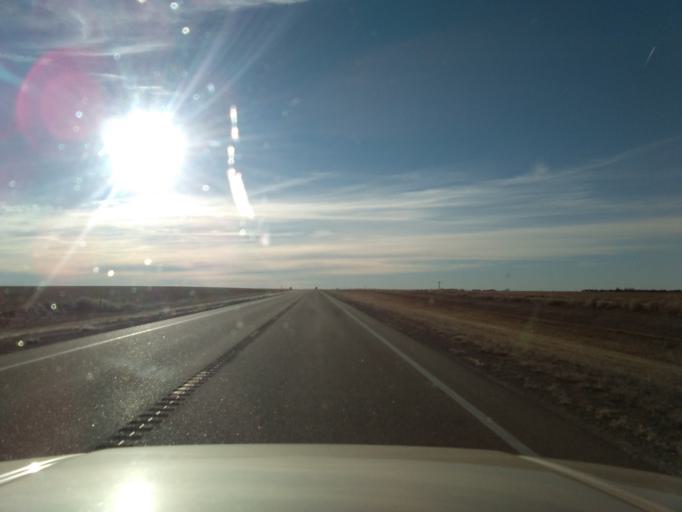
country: US
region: Kansas
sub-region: Sheridan County
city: Hoxie
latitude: 39.5176
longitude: -100.6293
